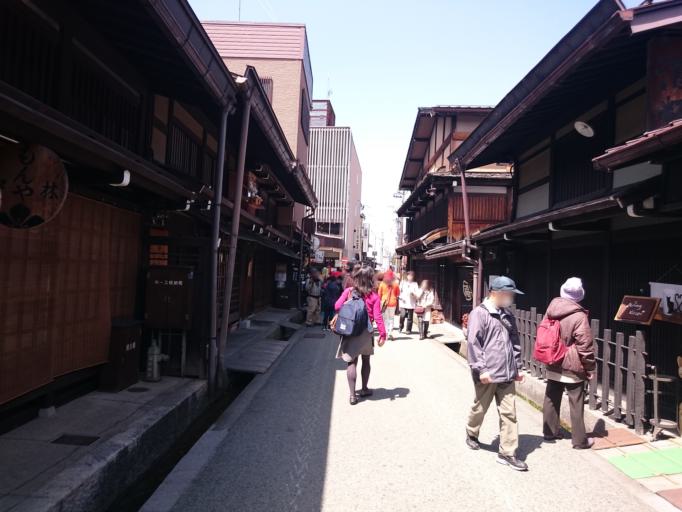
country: JP
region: Gifu
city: Takayama
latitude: 36.1431
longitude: 137.2590
